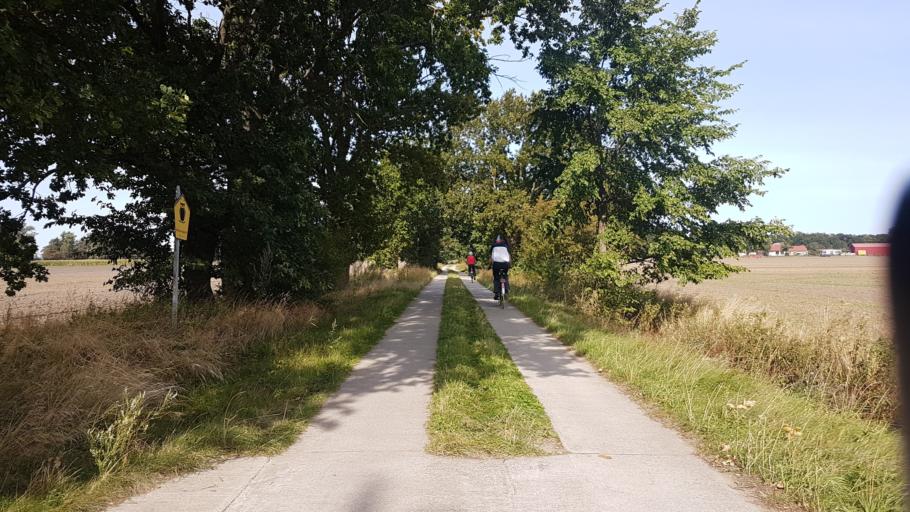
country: DE
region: Mecklenburg-Vorpommern
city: Samtens
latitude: 54.3994
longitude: 13.2596
